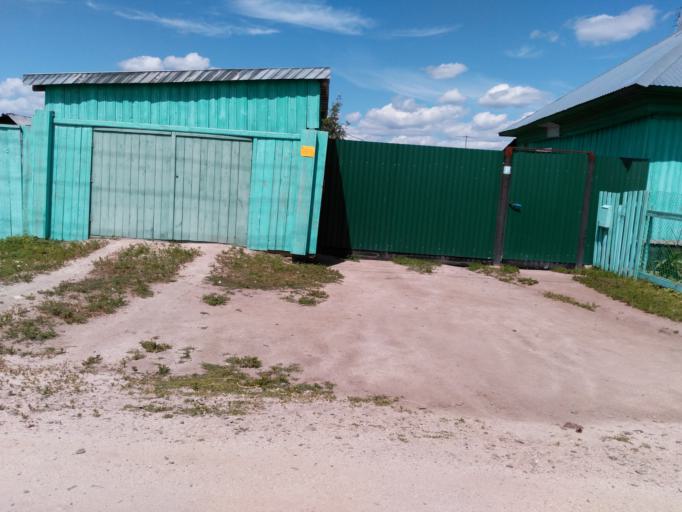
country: RU
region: Bashkortostan
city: Akhunovo
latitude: 54.2039
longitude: 59.5989
